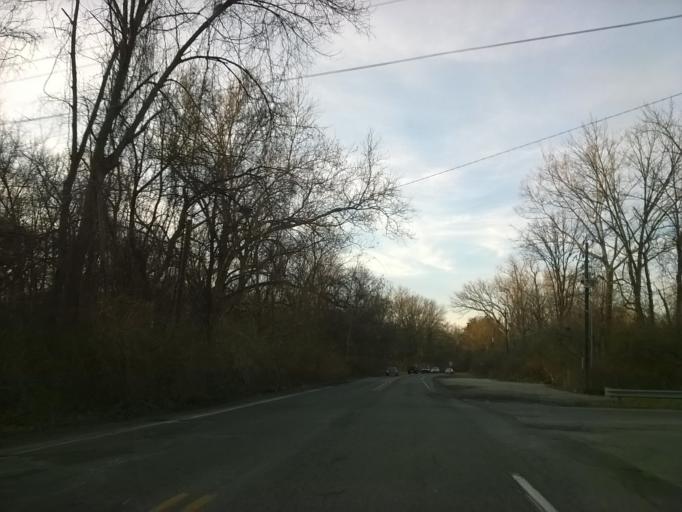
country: US
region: Indiana
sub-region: Marion County
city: Speedway
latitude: 39.8351
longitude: -86.2119
